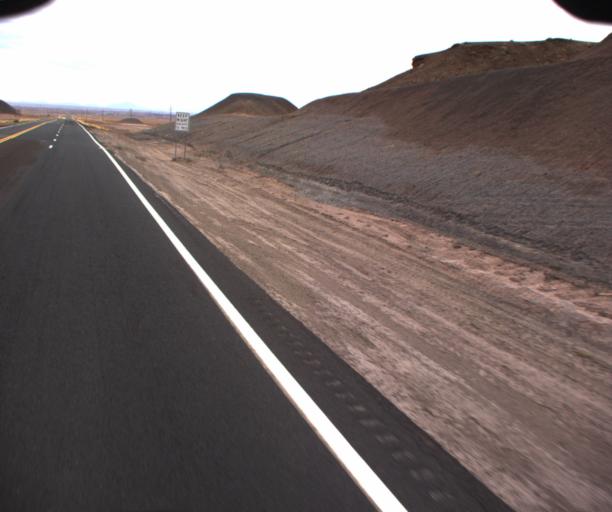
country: US
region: Arizona
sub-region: Coconino County
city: Tuba City
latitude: 35.9323
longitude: -111.4011
